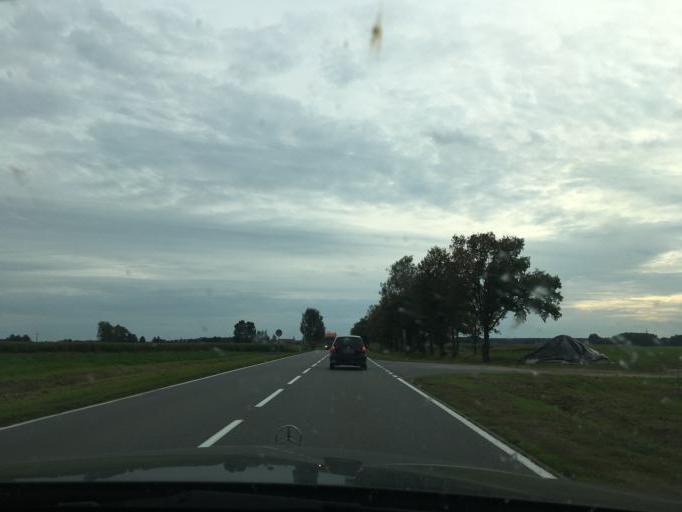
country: PL
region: Masovian Voivodeship
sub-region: Powiat ostrolecki
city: Czerwin
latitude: 52.9307
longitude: 21.8818
